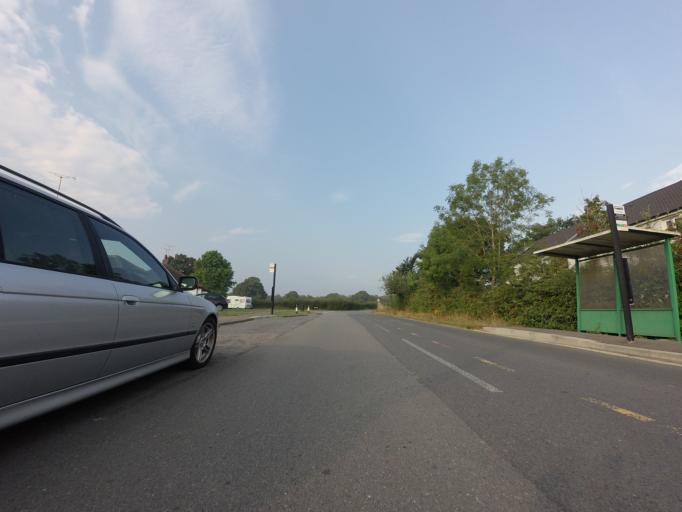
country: GB
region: England
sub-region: Kent
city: Ashford
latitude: 51.1075
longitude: 0.8125
